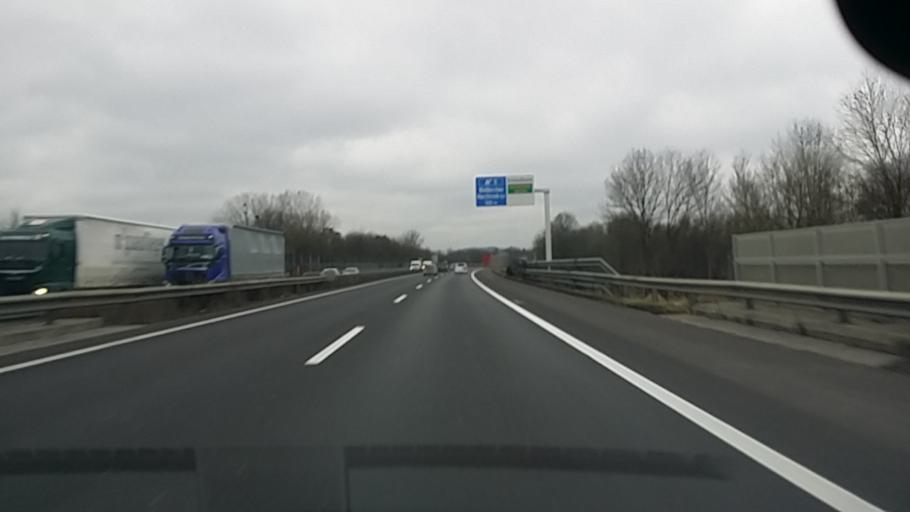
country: AT
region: Upper Austria
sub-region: Wels-Land
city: Marchtrenk
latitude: 48.1770
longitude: 14.1357
